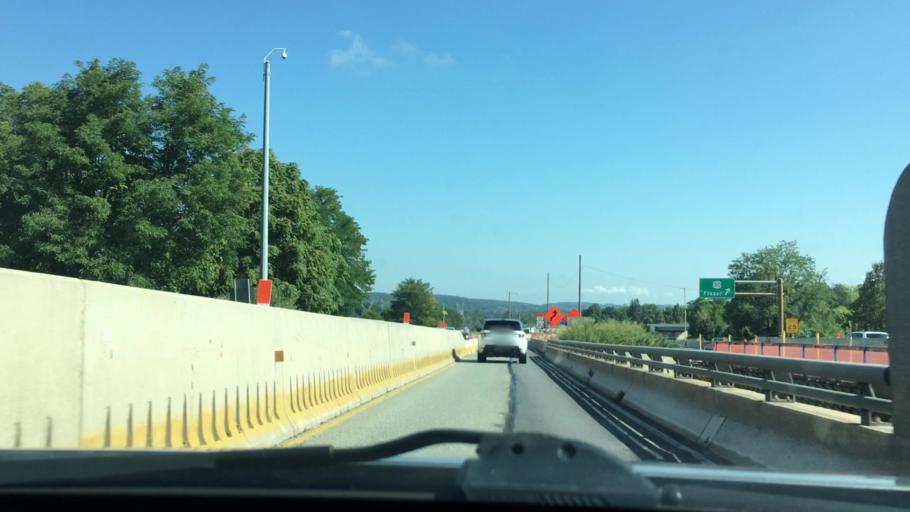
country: US
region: Pennsylvania
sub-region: Chester County
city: Exton
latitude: 40.0296
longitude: -75.5879
